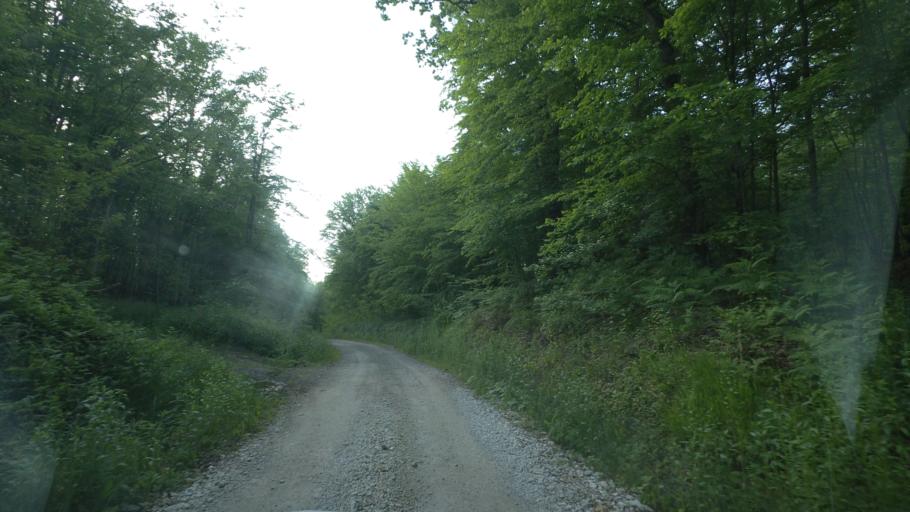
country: HR
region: Sisacko-Moslavacka
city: Gvozd
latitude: 45.3056
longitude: 15.9810
